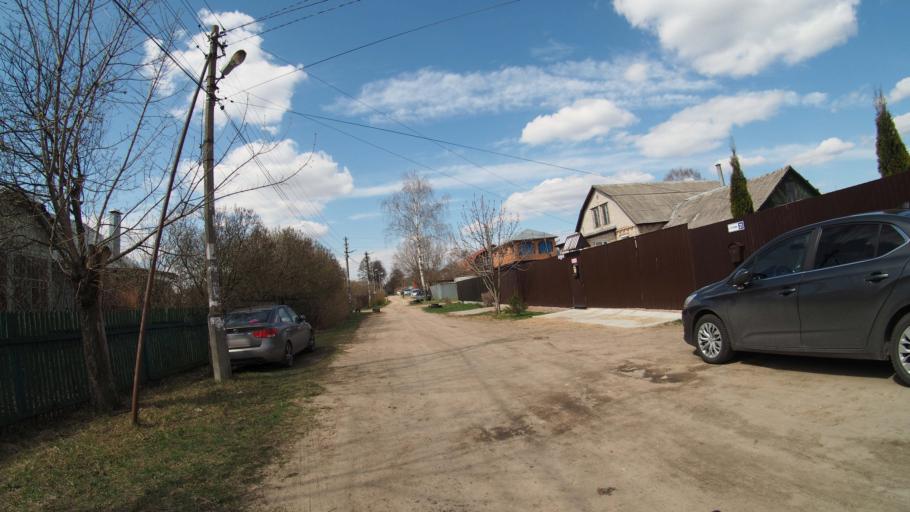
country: RU
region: Moskovskaya
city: Ramenskoye
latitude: 55.5630
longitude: 38.2149
